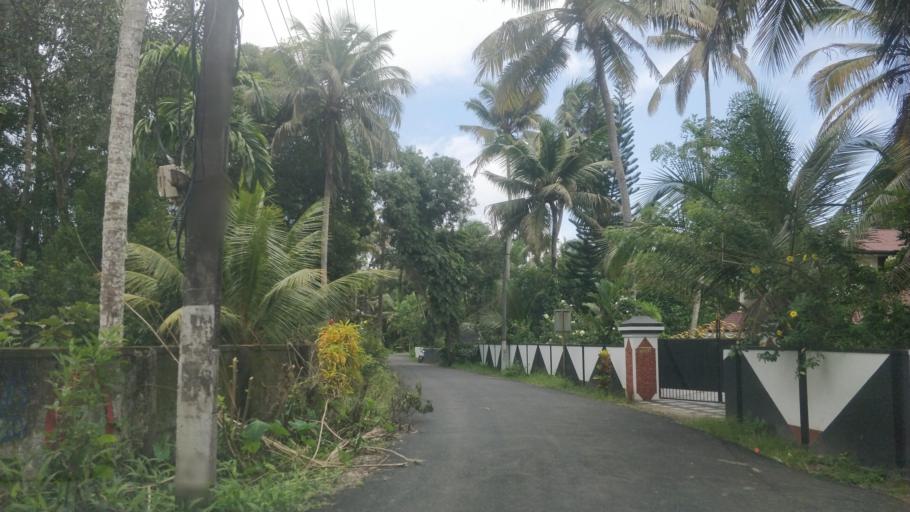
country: IN
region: Kerala
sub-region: Alappuzha
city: Shertallai
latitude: 9.6598
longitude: 76.3720
